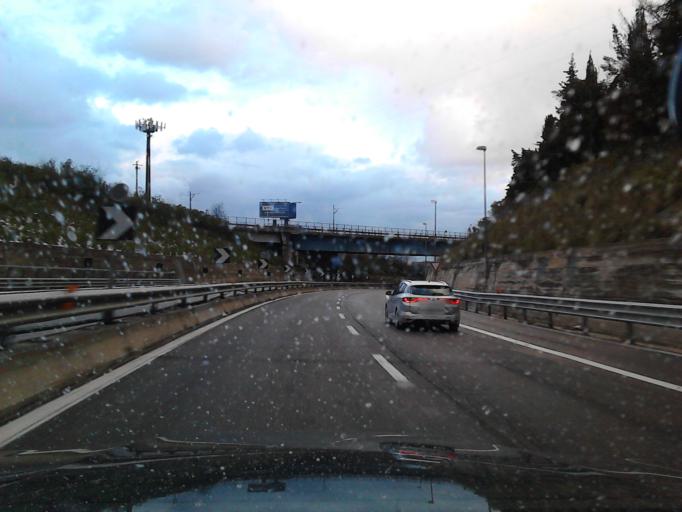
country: IT
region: Abruzzo
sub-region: Provincia di Chieti
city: Treglio
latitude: 42.2689
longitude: 14.4348
